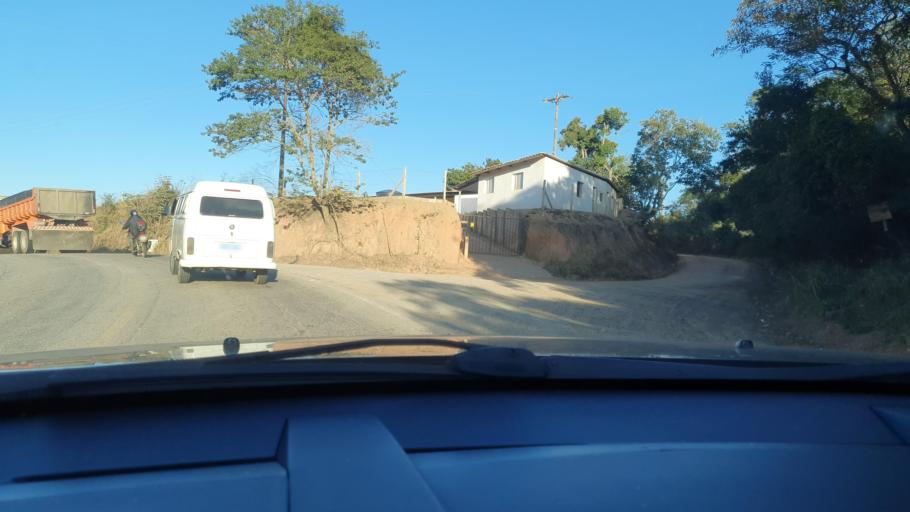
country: BR
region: Sao Paulo
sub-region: Piedade
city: Piedade
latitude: -23.7076
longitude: -47.3563
